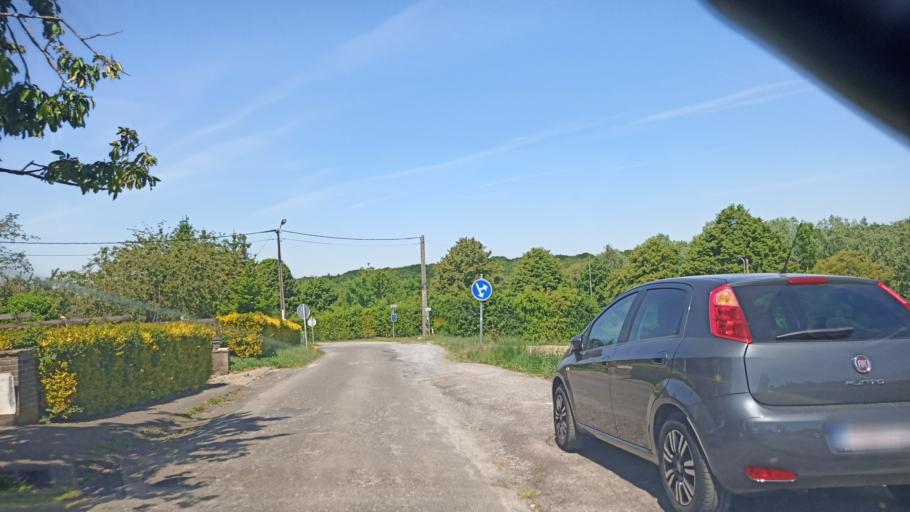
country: BE
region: Wallonia
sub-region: Province du Hainaut
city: Lobbes
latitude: 50.3297
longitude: 4.2543
